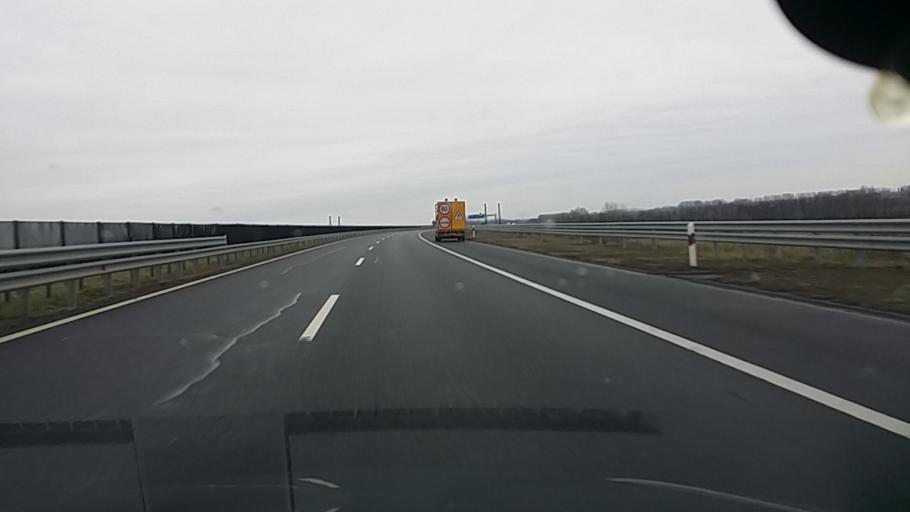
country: HU
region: Szabolcs-Szatmar-Bereg
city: Nyiregyhaza
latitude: 47.8835
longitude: 21.7192
